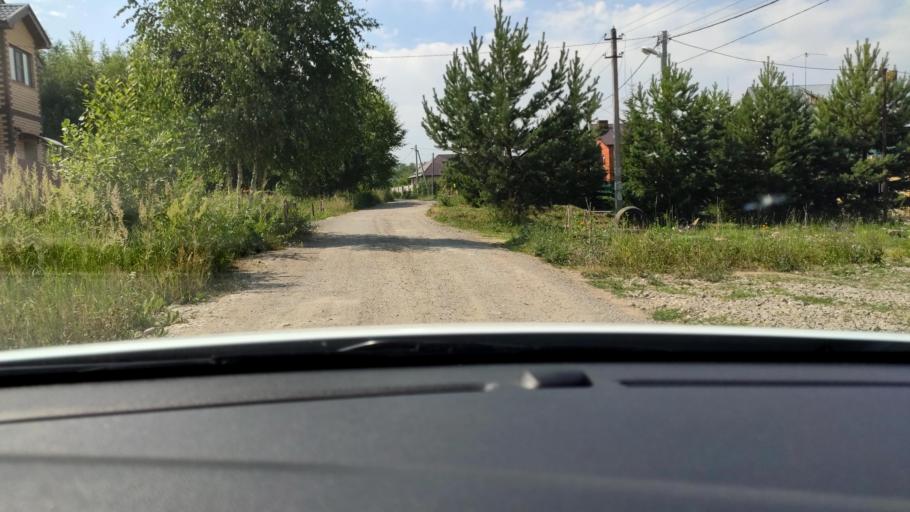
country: RU
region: Tatarstan
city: Stolbishchi
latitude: 55.7438
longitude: 49.2528
